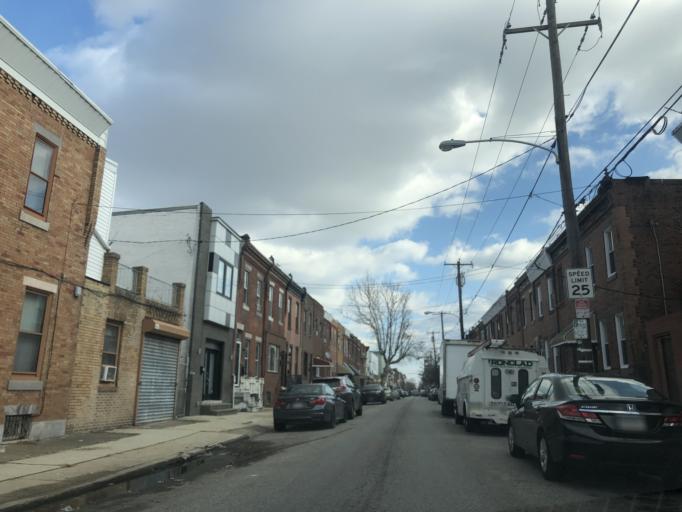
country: US
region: Pennsylvania
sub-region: Philadelphia County
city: Philadelphia
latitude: 39.9280
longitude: -75.1786
